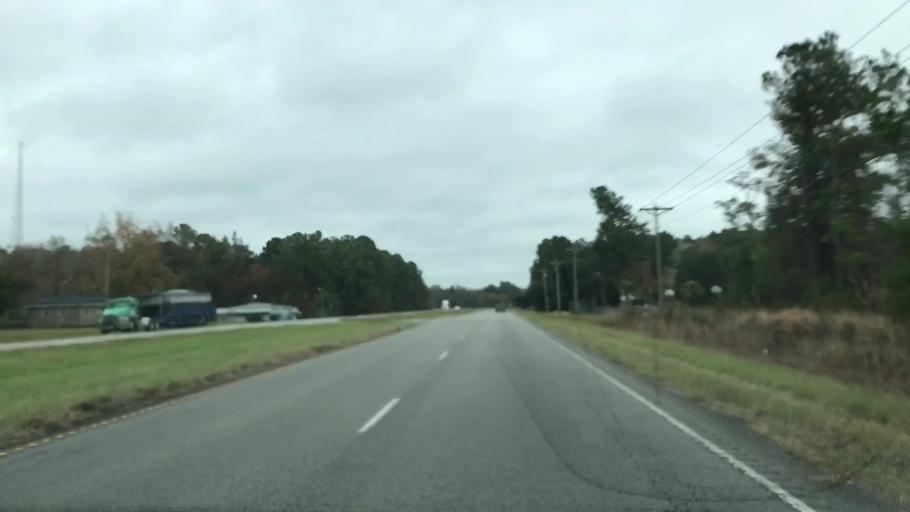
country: US
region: South Carolina
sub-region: Charleston County
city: Awendaw
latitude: 33.0235
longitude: -79.6303
